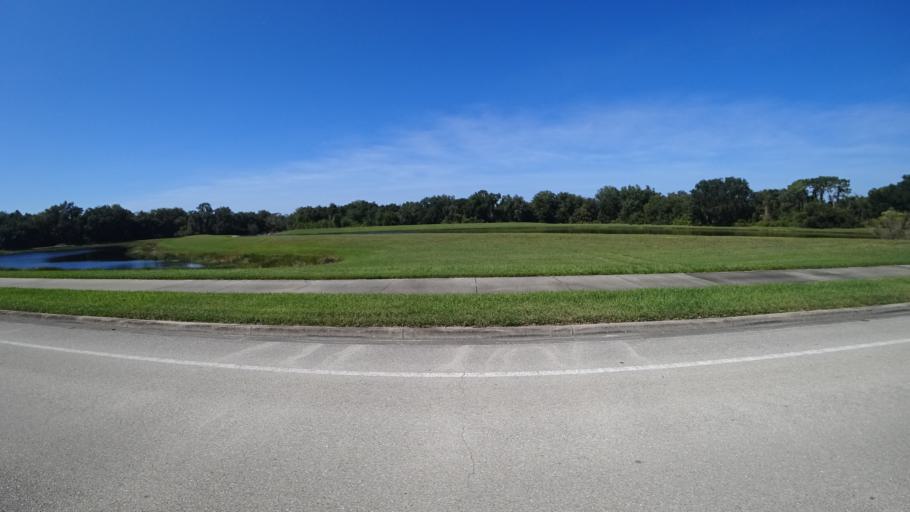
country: US
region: Florida
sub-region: Sarasota County
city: The Meadows
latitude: 27.4145
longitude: -82.4264
